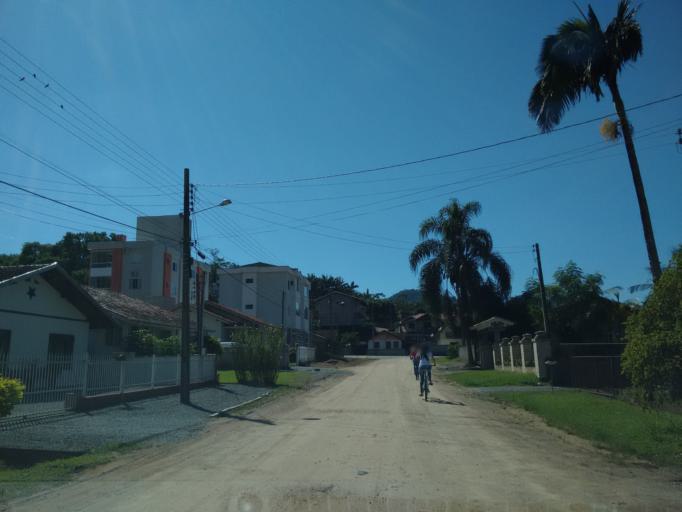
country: BR
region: Santa Catarina
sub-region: Pomerode
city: Pomerode
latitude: -26.7502
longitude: -49.1797
